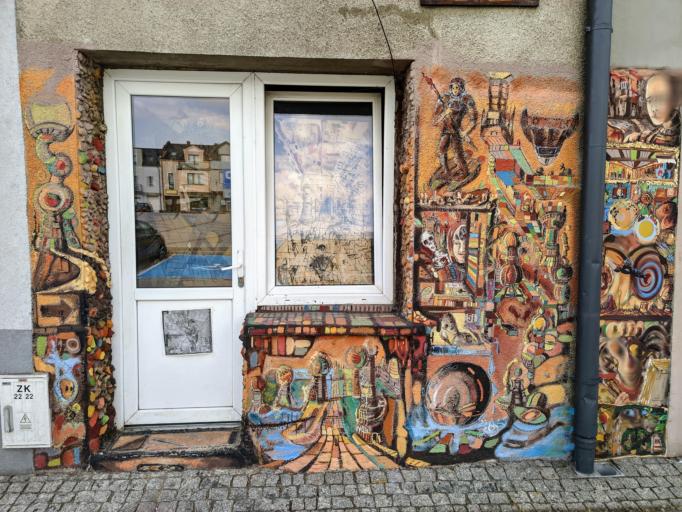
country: PL
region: Silesian Voivodeship
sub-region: Powiat klobucki
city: Klobuck
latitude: 50.9049
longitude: 18.9364
